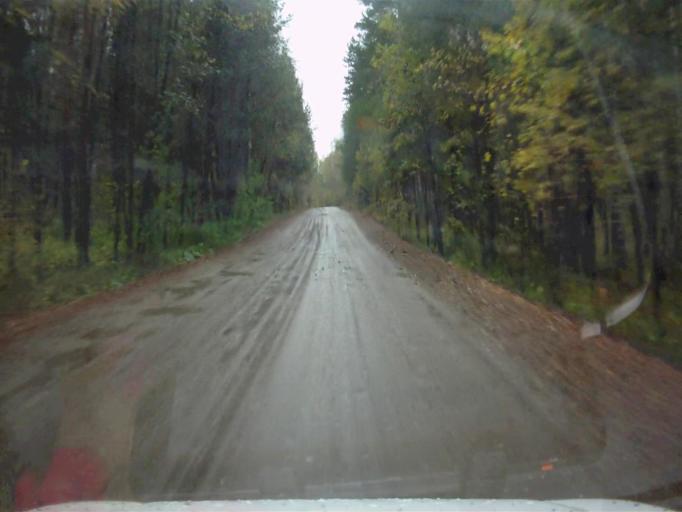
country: RU
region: Chelyabinsk
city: Kyshtym
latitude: 55.8391
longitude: 60.4865
